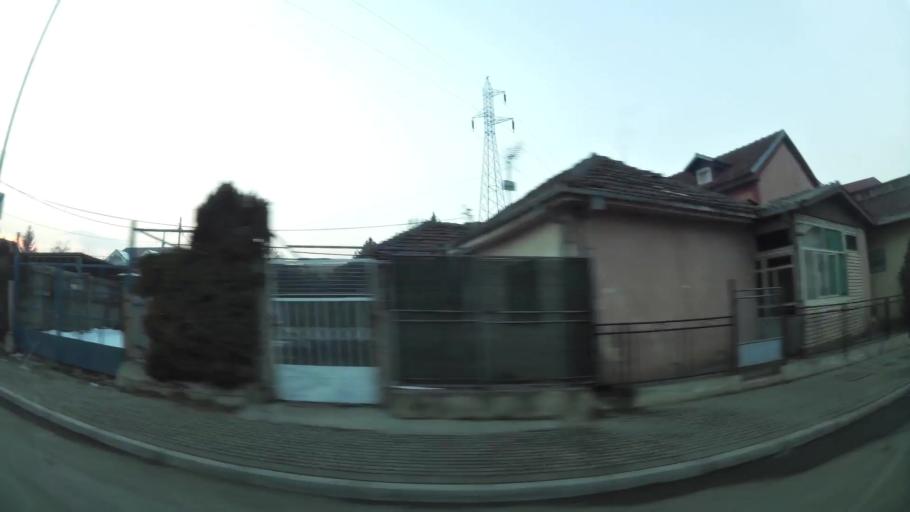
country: MK
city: Creshevo
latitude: 42.0030
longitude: 21.5035
